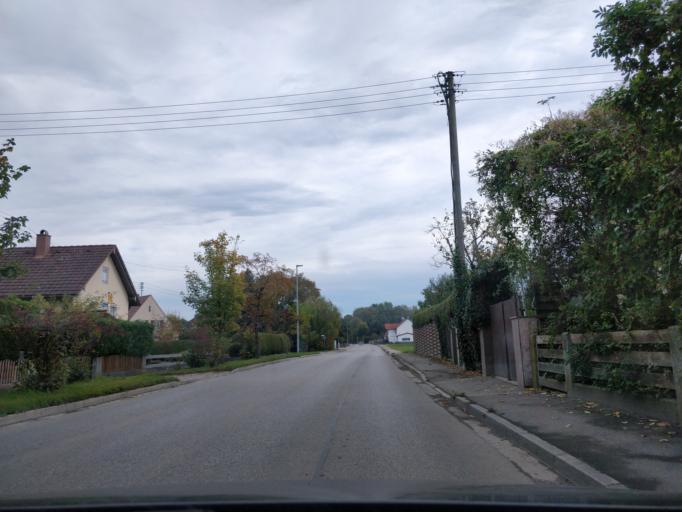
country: DE
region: Bavaria
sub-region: Swabia
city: Wiedergeltingen
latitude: 48.0392
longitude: 10.6769
